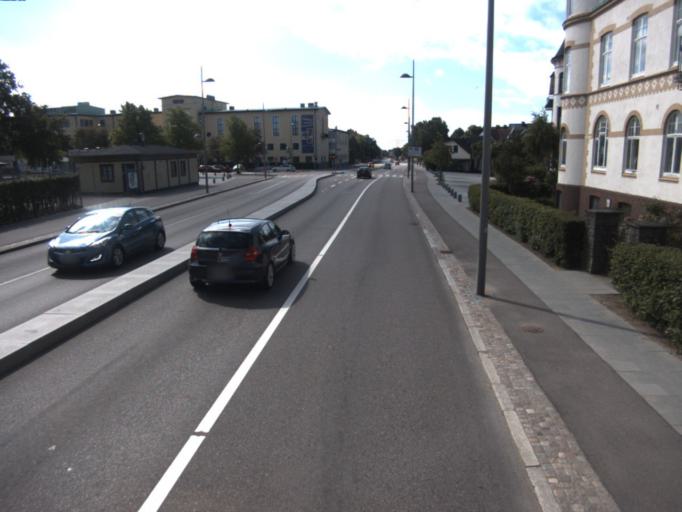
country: SE
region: Skane
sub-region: Helsingborg
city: Helsingborg
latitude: 56.0493
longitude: 12.7056
